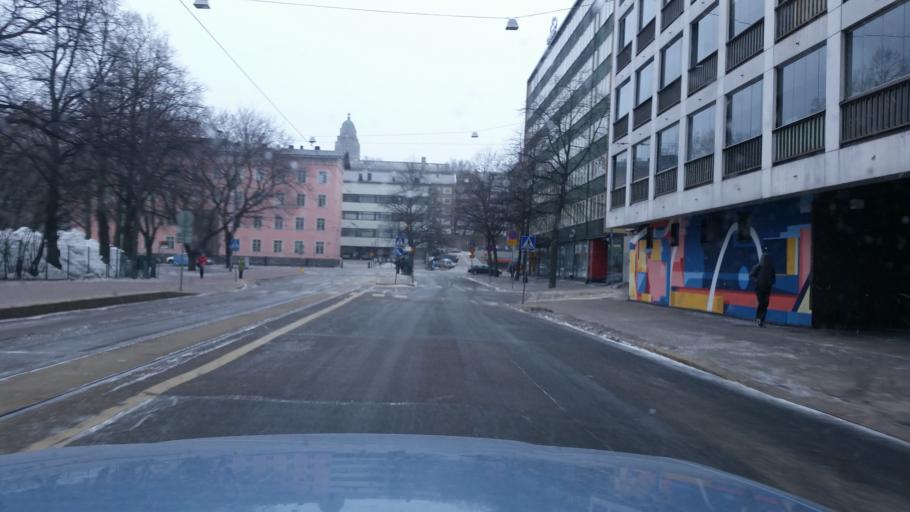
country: FI
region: Uusimaa
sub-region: Helsinki
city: Helsinki
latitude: 60.1875
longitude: 24.9483
